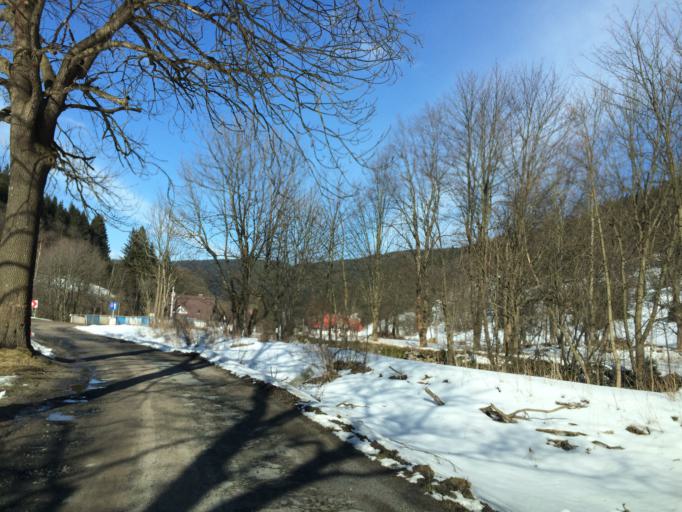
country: CZ
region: Olomoucky
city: Vapenna
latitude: 50.2669
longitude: 17.0029
